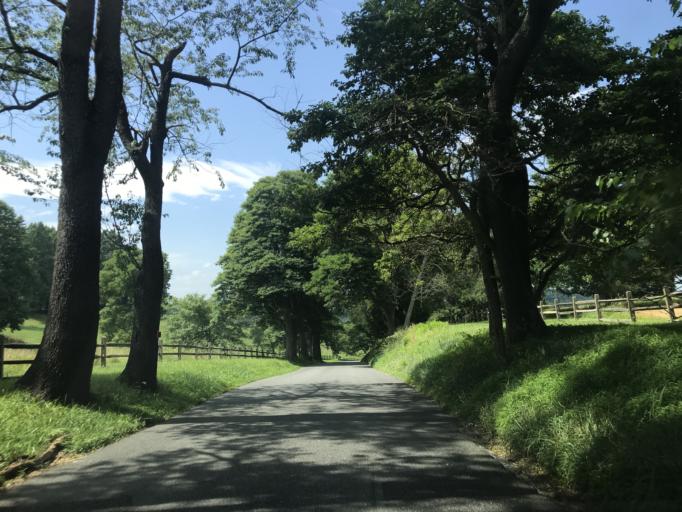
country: US
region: Delaware
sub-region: New Castle County
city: Hockessin
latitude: 39.7924
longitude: -75.6563
